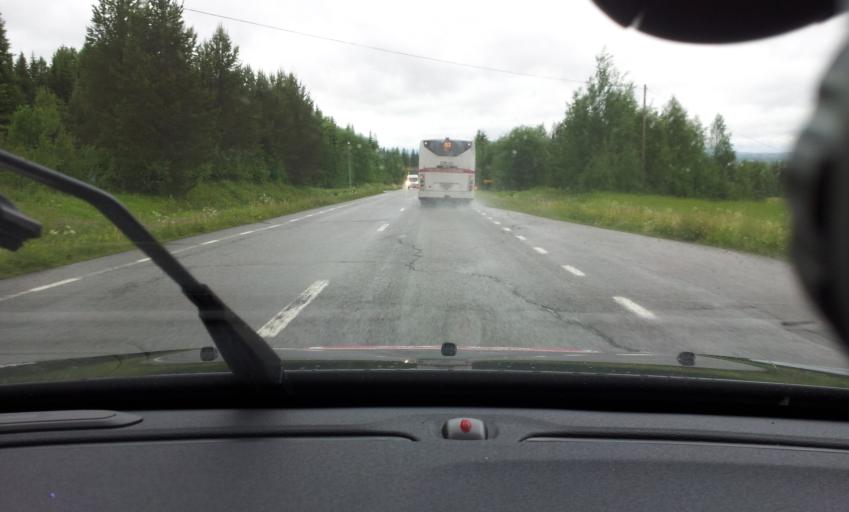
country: SE
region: Jaemtland
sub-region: Krokoms Kommun
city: Krokom
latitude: 63.5825
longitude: 14.6349
